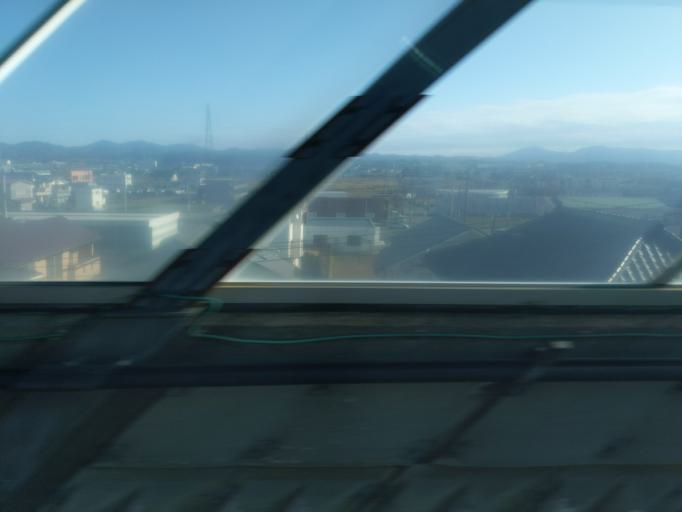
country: JP
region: Fukushima
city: Koriyama
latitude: 37.3704
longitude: 140.3803
